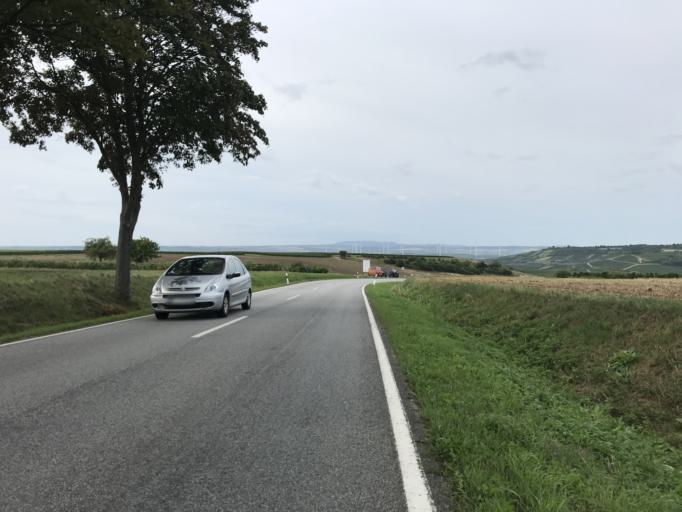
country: DE
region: Rheinland-Pfalz
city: Vendersheim
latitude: 49.8729
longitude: 8.0548
